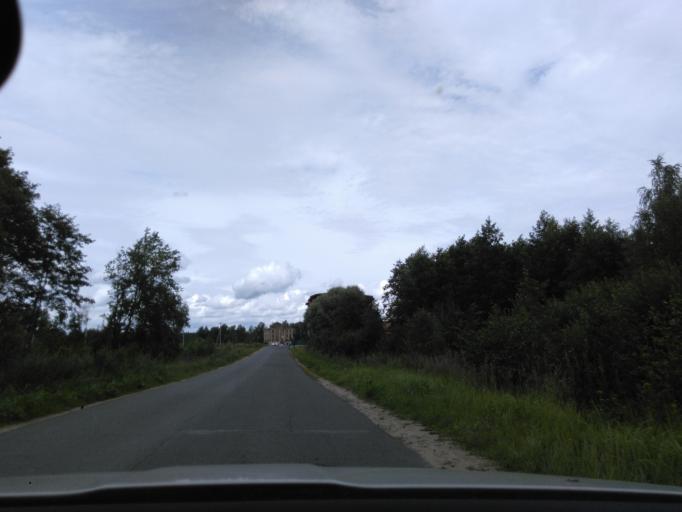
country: RU
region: Tverskaya
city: Konakovo
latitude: 56.6729
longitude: 36.7125
